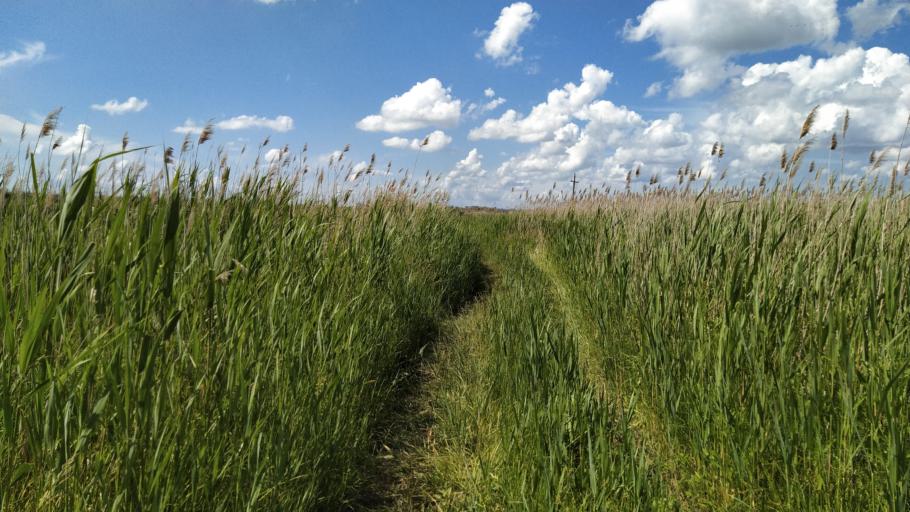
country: RU
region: Rostov
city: Bataysk
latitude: 47.1365
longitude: 39.6700
